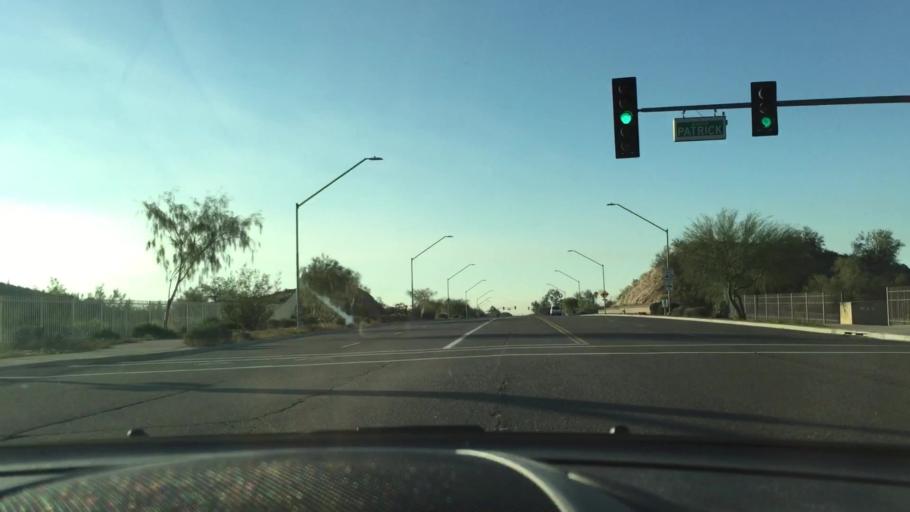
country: US
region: Arizona
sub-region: Maricopa County
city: Peoria
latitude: 33.6926
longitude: -112.2031
